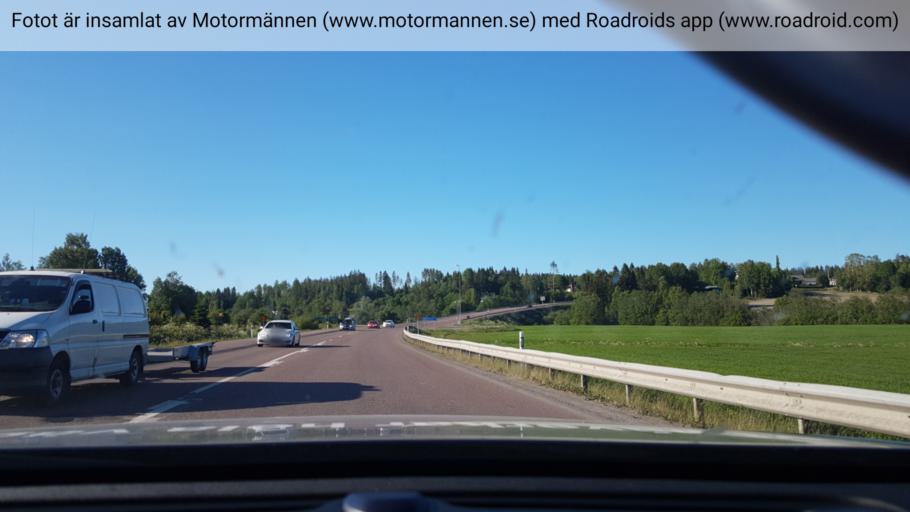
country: SE
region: Vaesternorrland
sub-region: Haernoesands Kommun
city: Haernoesand
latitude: 62.6842
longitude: 17.8470
